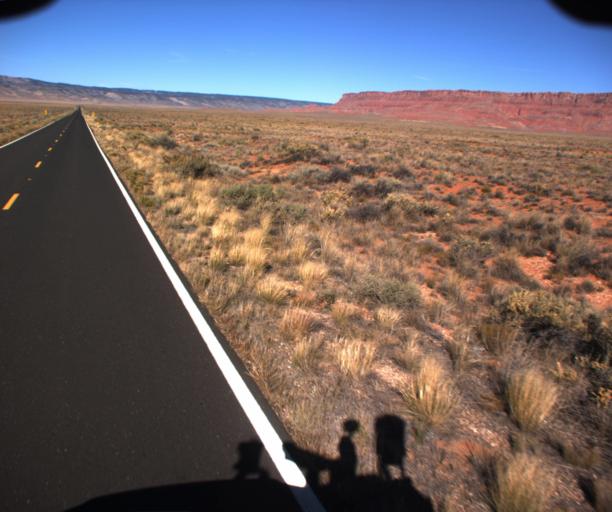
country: US
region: Arizona
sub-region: Coconino County
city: Page
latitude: 36.6990
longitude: -111.9216
